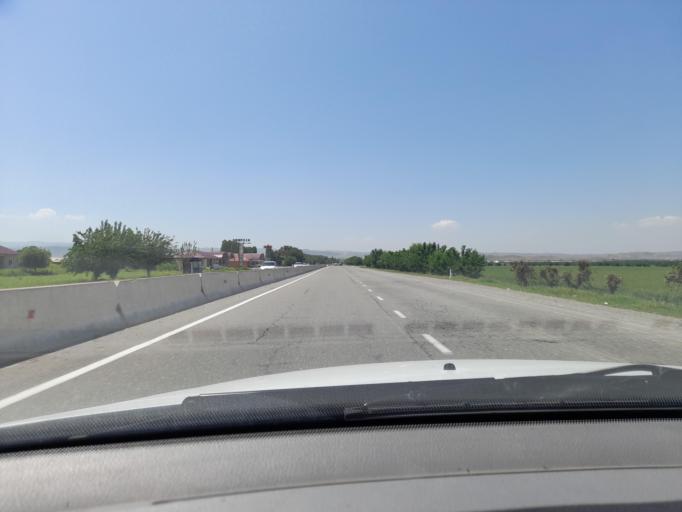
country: UZ
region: Jizzax
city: Jizzax
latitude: 40.0750
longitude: 67.9070
